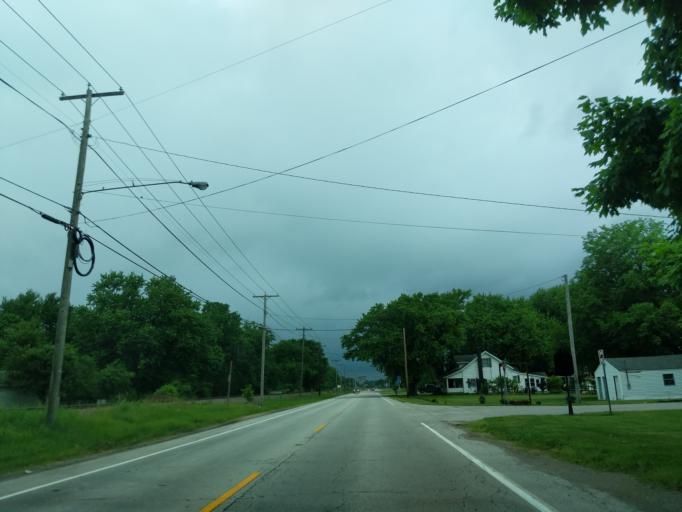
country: US
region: Indiana
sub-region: Delaware County
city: Daleville
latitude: 40.1209
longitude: -85.5612
